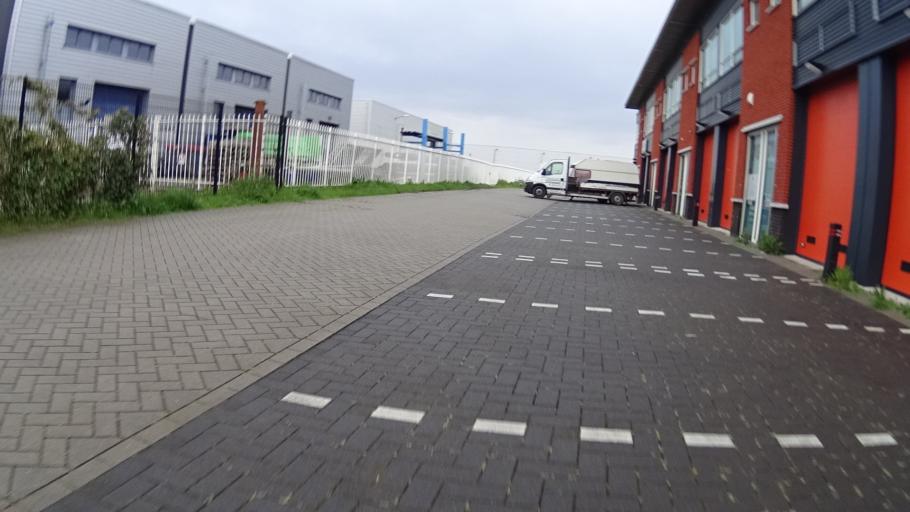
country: NL
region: South Holland
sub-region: Gemeente Brielle
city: Brielle
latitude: 51.8947
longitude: 4.1911
